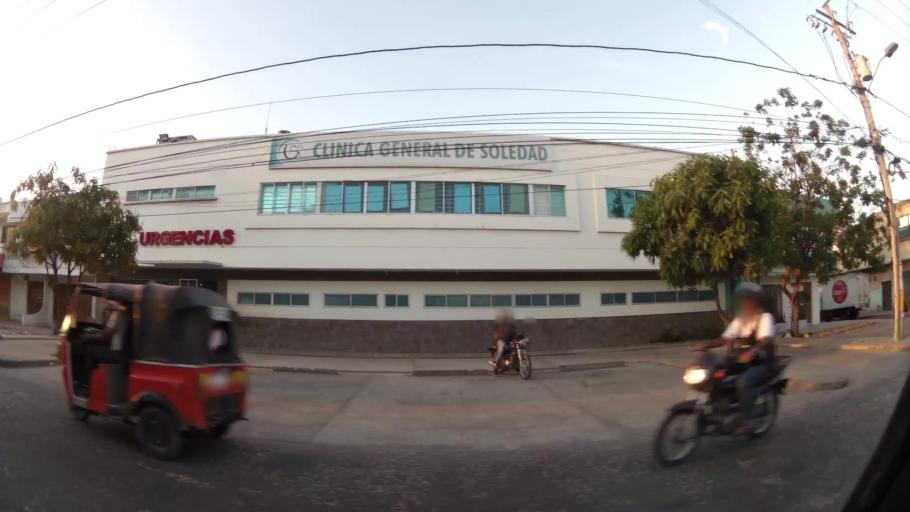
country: CO
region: Atlantico
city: Soledad
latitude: 10.9280
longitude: -74.7751
